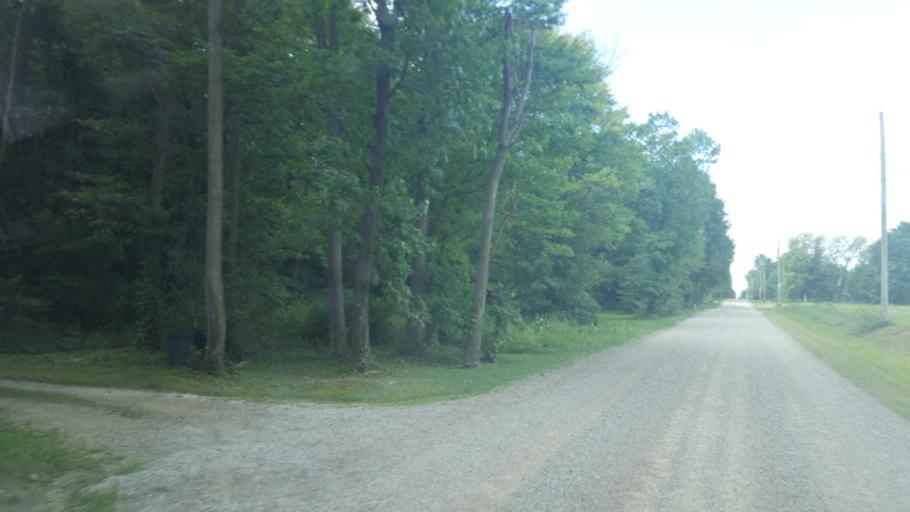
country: US
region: Ohio
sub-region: Morrow County
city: Mount Gilead
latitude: 40.4318
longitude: -82.7530
